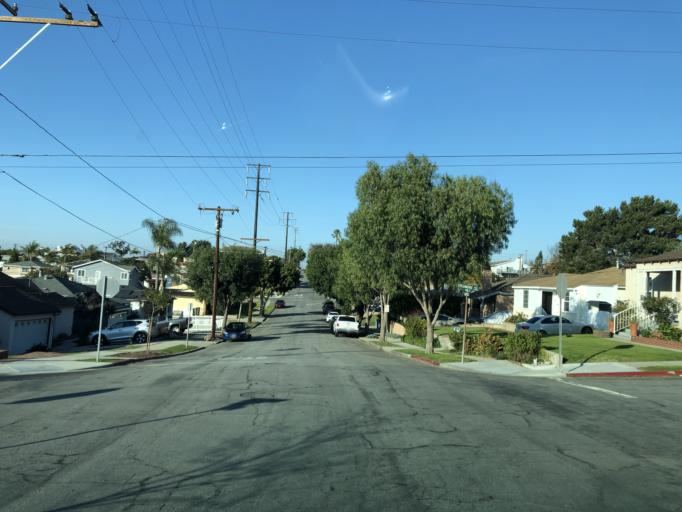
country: US
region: California
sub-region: Los Angeles County
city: El Segundo
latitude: 33.9277
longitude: -118.4136
